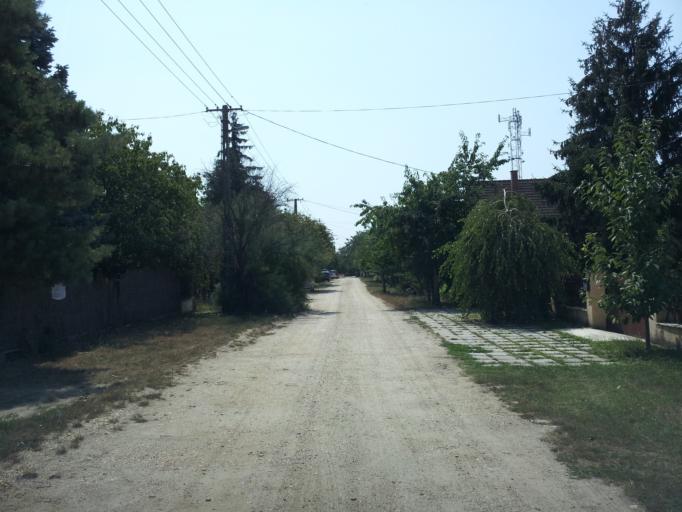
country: HU
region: Pest
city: Dunavarsany
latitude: 47.2668
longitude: 19.0689
